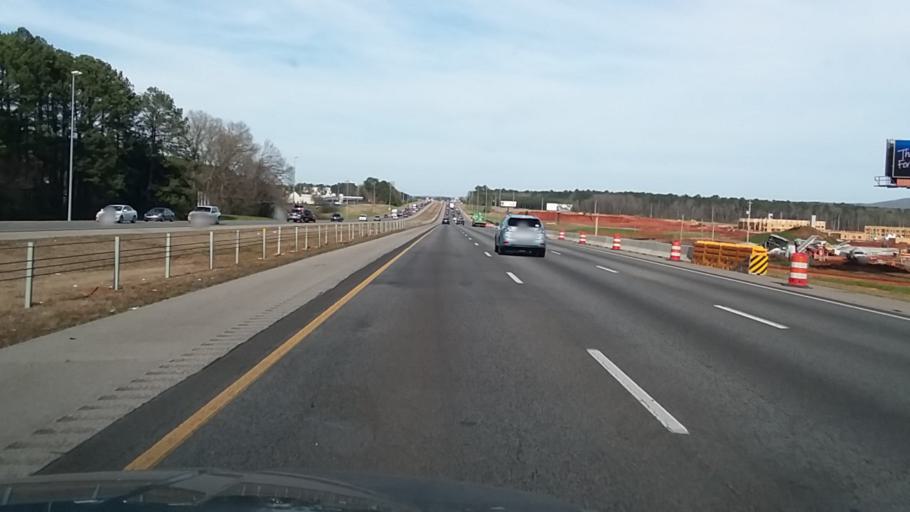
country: US
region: Alabama
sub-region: Madison County
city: Madison
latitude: 34.6846
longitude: -86.7269
